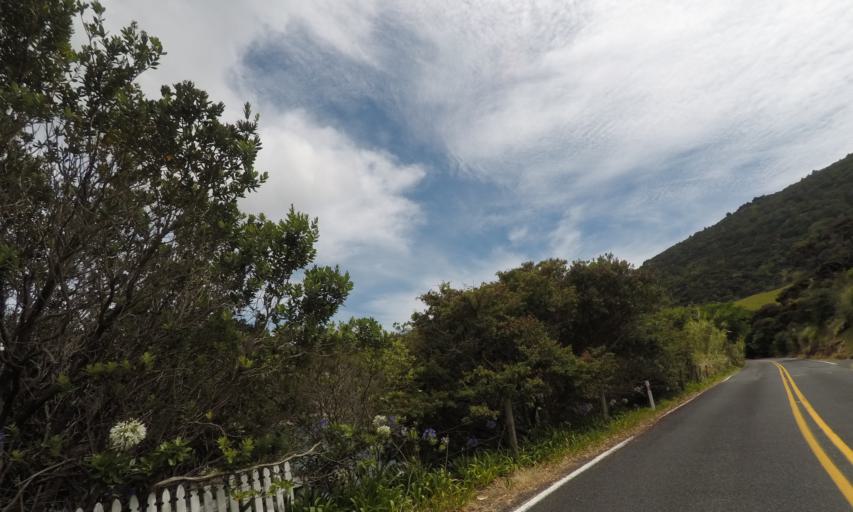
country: NZ
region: Northland
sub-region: Whangarei
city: Ruakaka
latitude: -35.8334
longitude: 174.5311
